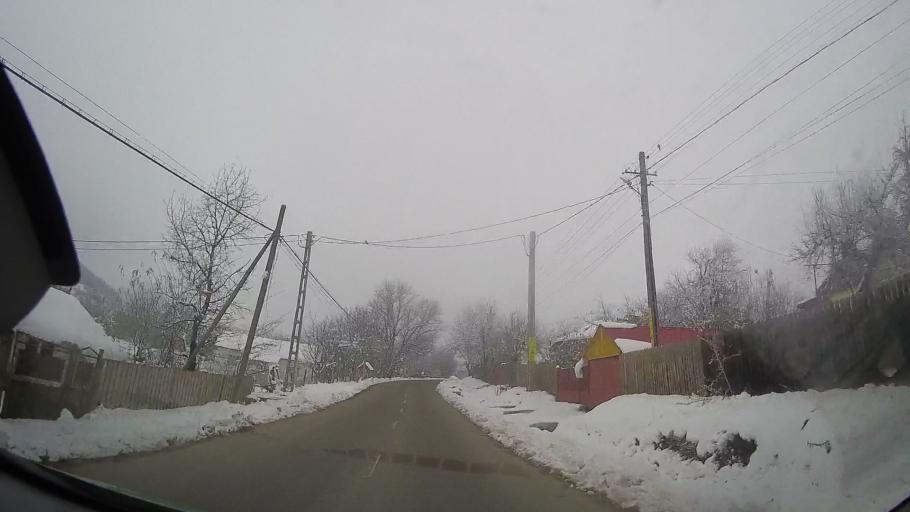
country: RO
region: Neamt
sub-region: Comuna Bozieni
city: Bozieni
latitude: 46.8396
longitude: 27.1490
